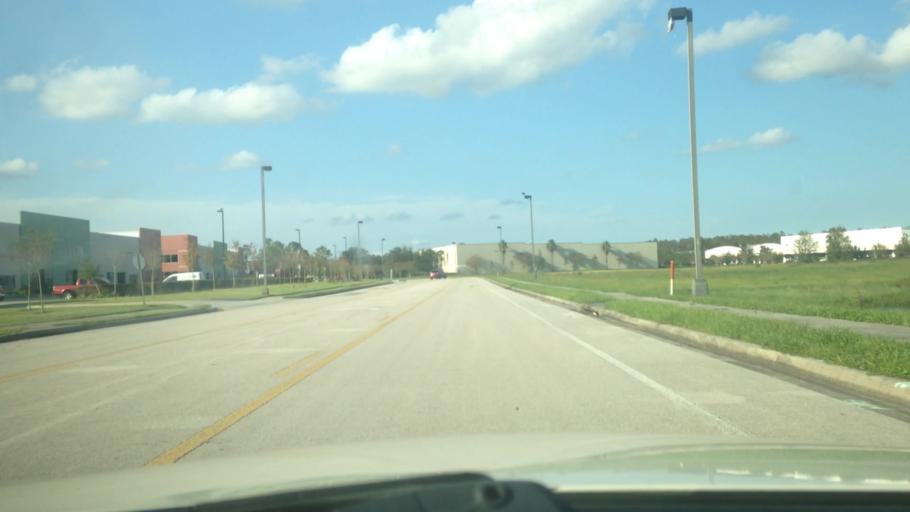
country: US
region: Florida
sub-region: Orange County
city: Conway
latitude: 28.4558
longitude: -81.2962
